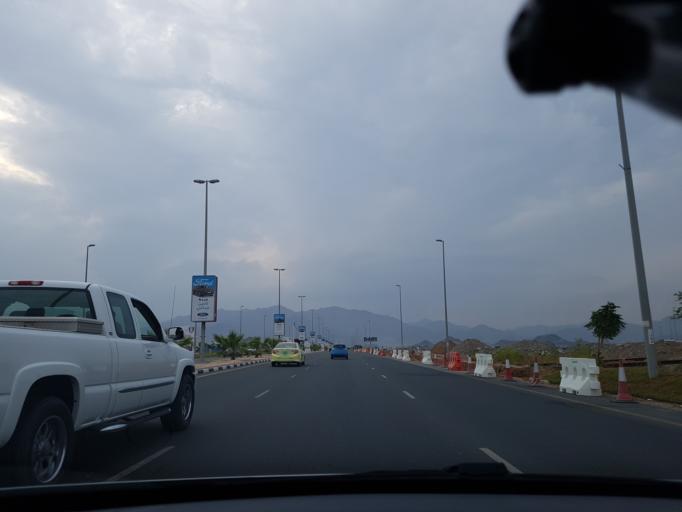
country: AE
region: Al Fujayrah
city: Al Fujayrah
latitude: 25.1226
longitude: 56.3037
